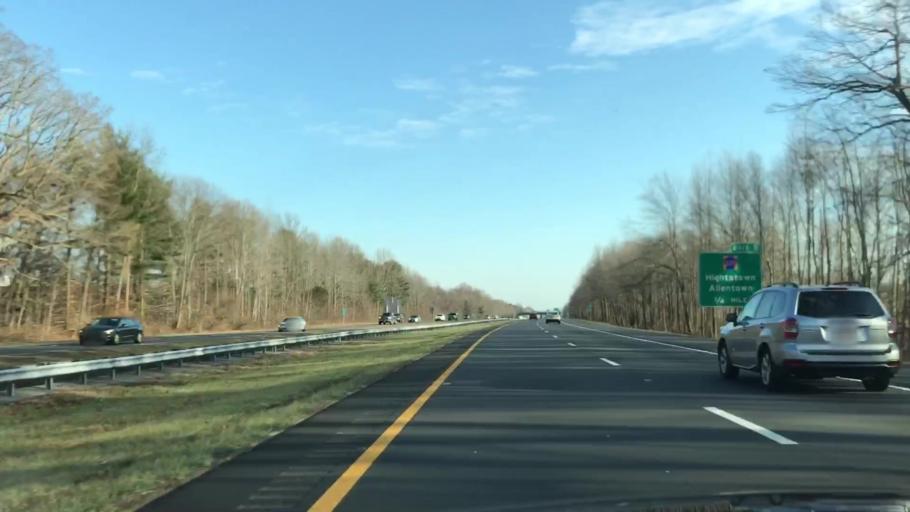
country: US
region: New Jersey
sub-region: Monmouth County
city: Allentown
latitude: 40.1895
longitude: -74.5813
